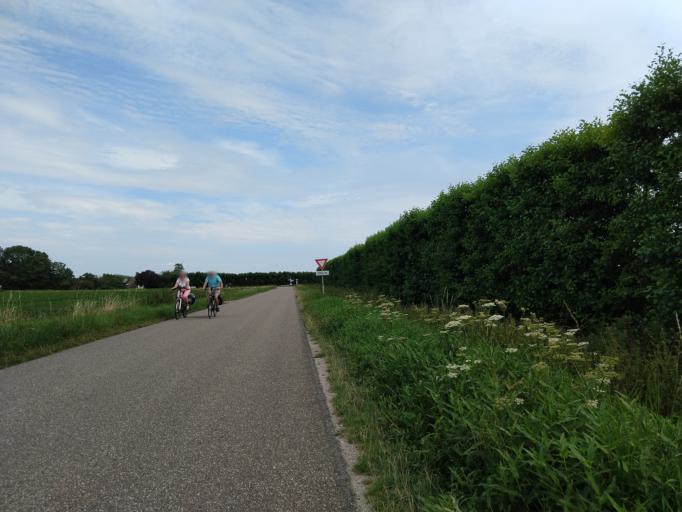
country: NL
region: Zeeland
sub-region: Gemeente Veere
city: Veere
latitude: 51.4900
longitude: 3.7077
